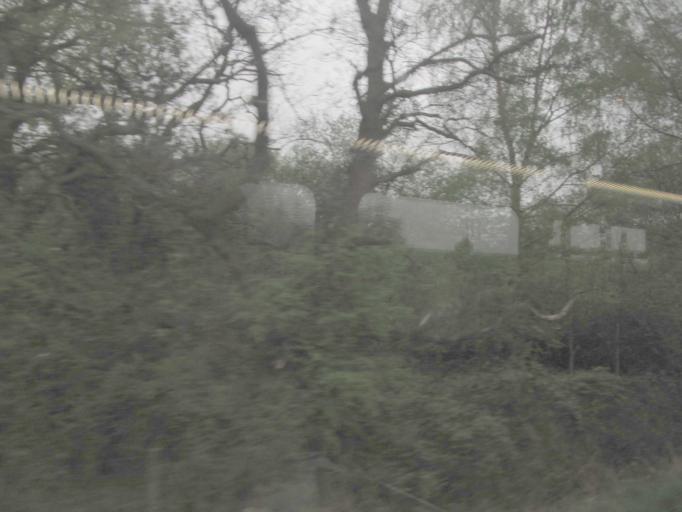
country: GB
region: England
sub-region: Bracknell Forest
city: Sandhurst
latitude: 51.3340
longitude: -0.7807
